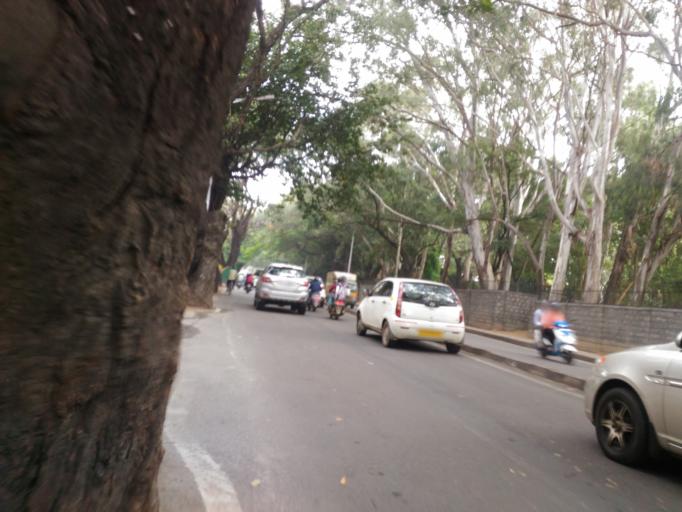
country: IN
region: Karnataka
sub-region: Bangalore Urban
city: Bangalore
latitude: 12.9565
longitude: 77.6057
